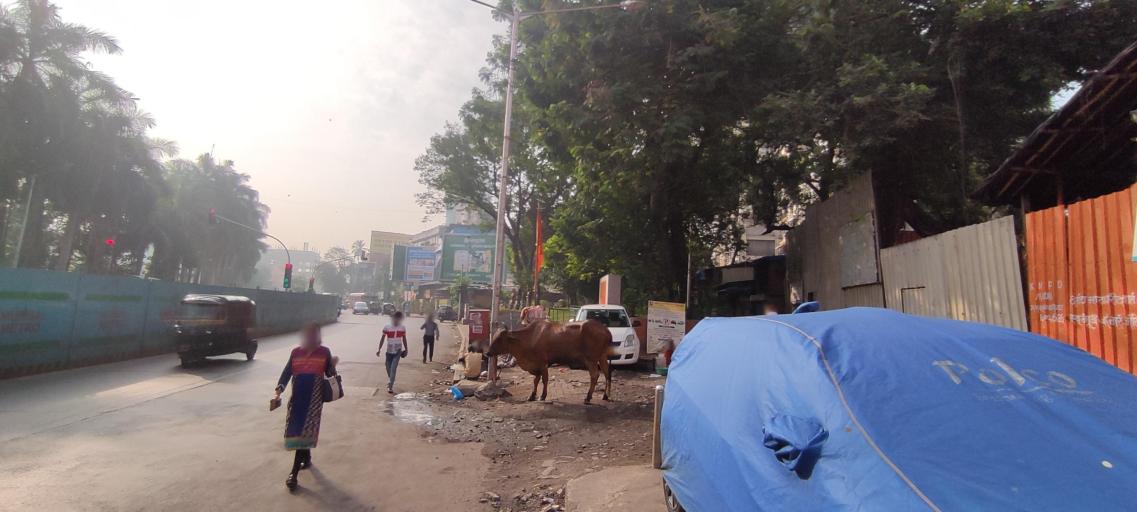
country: IN
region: Maharashtra
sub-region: Mumbai Suburban
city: Mumbai
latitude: 19.0572
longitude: 72.8366
